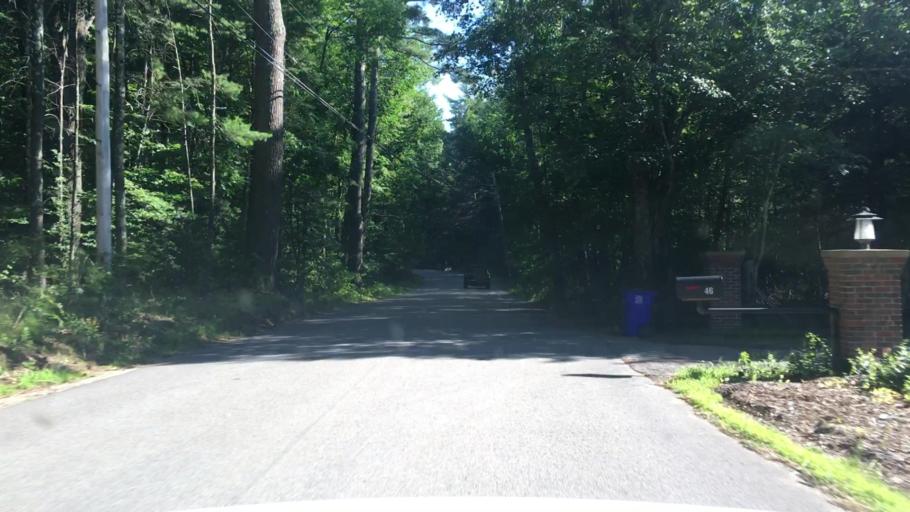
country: US
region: New Hampshire
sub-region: Rockingham County
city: Exeter
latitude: 43.0252
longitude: -70.9721
